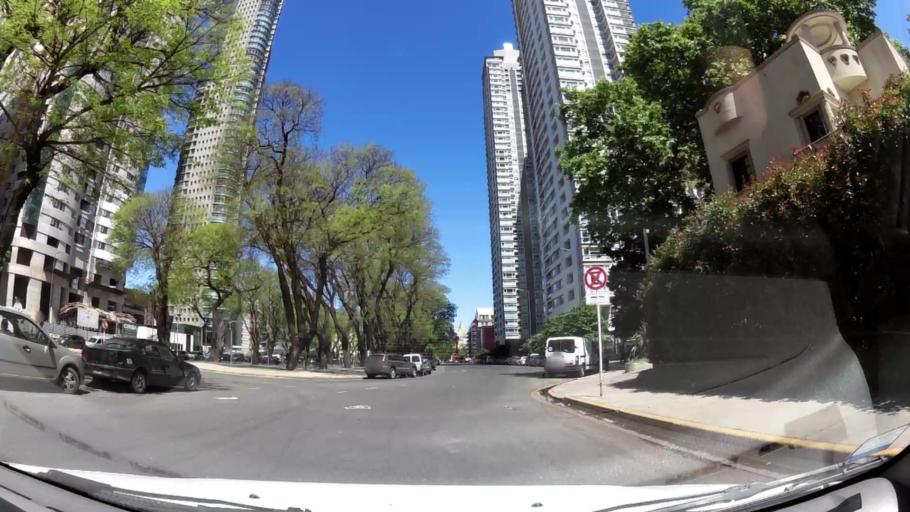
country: AR
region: Buenos Aires F.D.
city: Buenos Aires
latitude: -34.6115
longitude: -58.3597
